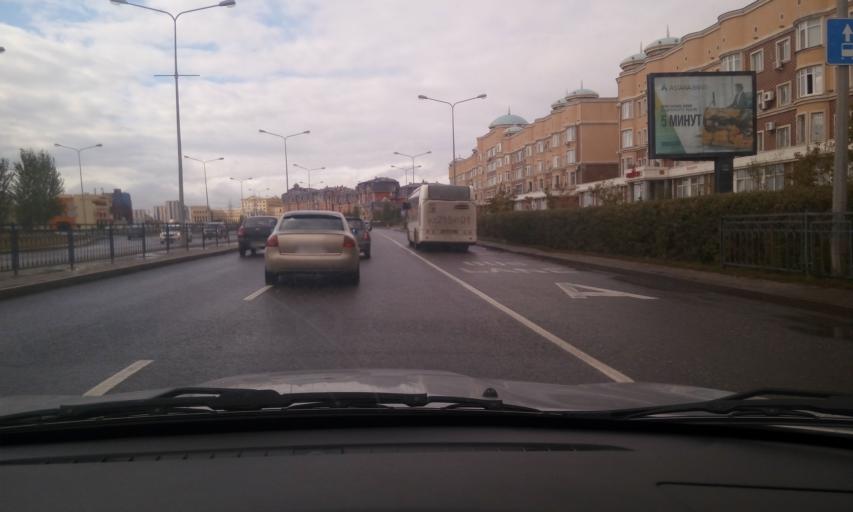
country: KZ
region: Astana Qalasy
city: Astana
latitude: 51.1482
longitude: 71.3921
